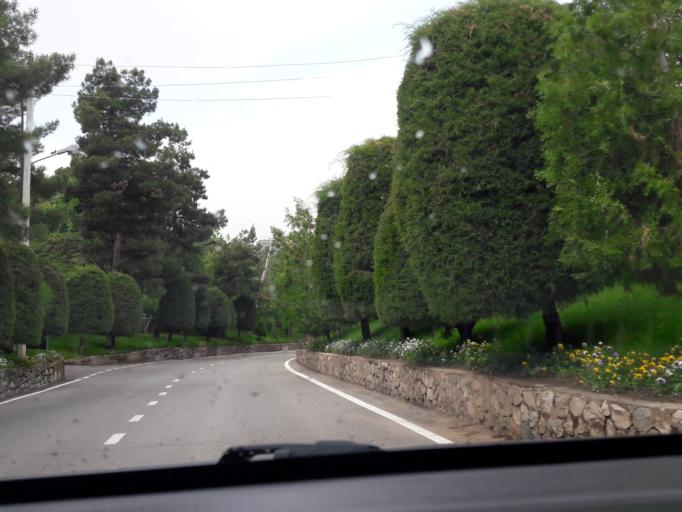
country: TJ
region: Dushanbe
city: Dushanbe
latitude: 38.5799
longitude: 68.8074
